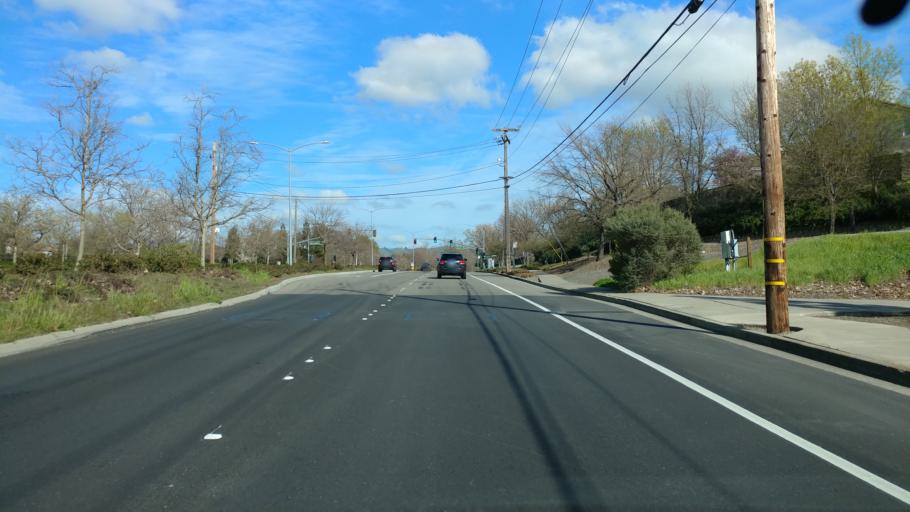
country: US
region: California
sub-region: Contra Costa County
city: Blackhawk
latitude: 37.7992
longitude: -121.9057
